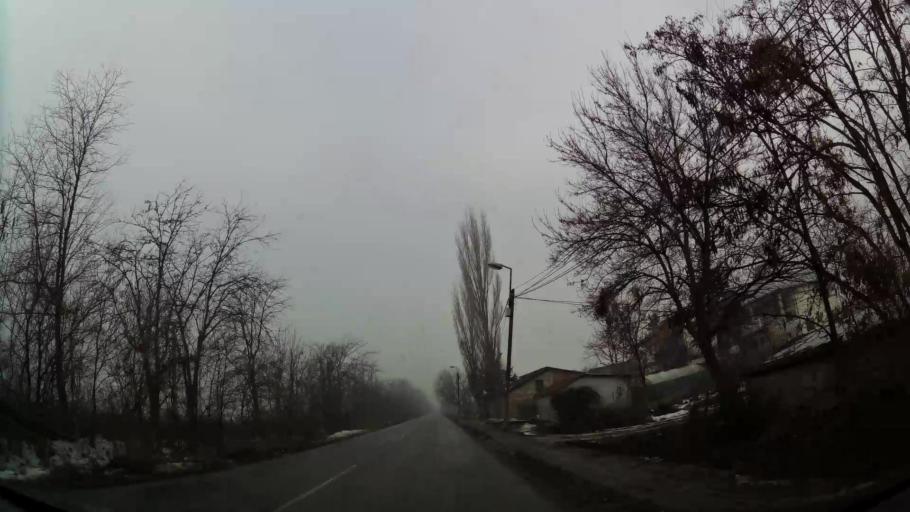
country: MK
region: Ilinden
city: Idrizovo
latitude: 41.9554
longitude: 21.5748
